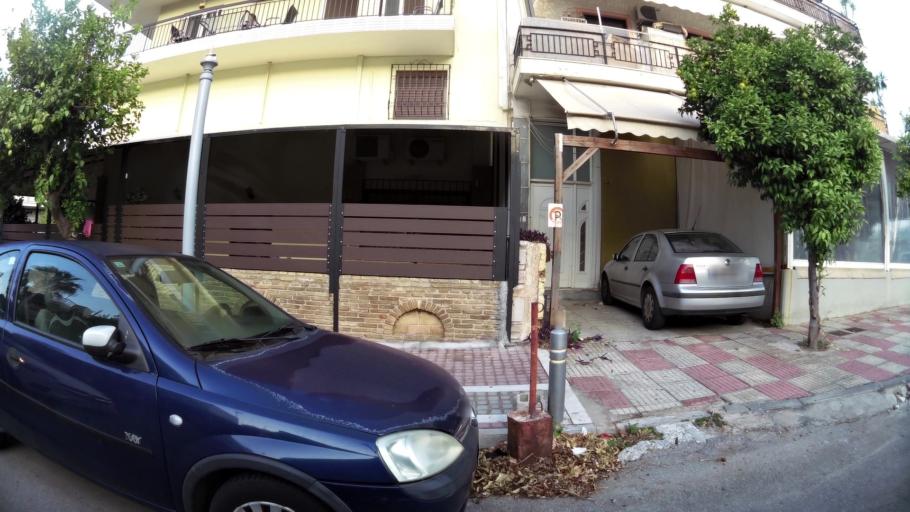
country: GR
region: Attica
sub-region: Nomarchia Athinas
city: Ymittos
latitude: 37.9485
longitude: 23.7443
